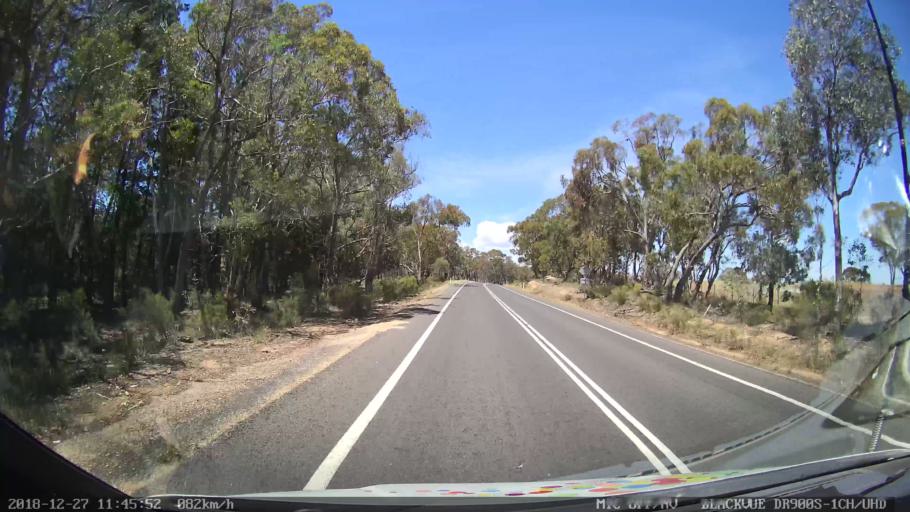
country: AU
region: New South Wales
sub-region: Bathurst Regional
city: Perthville
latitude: -33.5855
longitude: 149.4647
